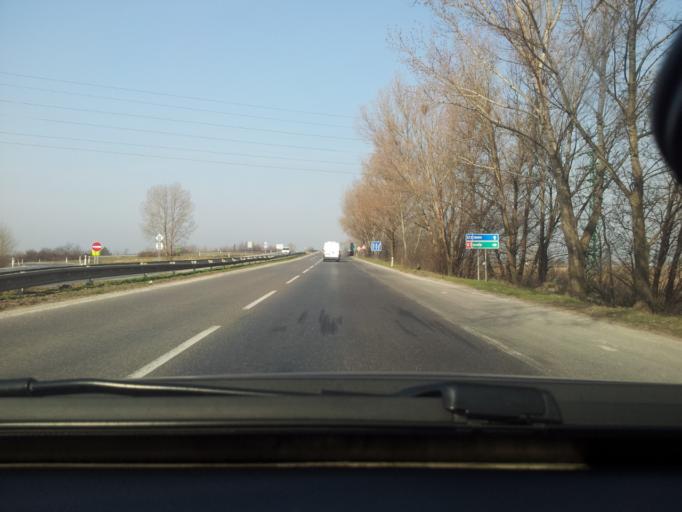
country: SK
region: Trnavsky
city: Leopoldov
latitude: 48.4376
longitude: 17.7453
